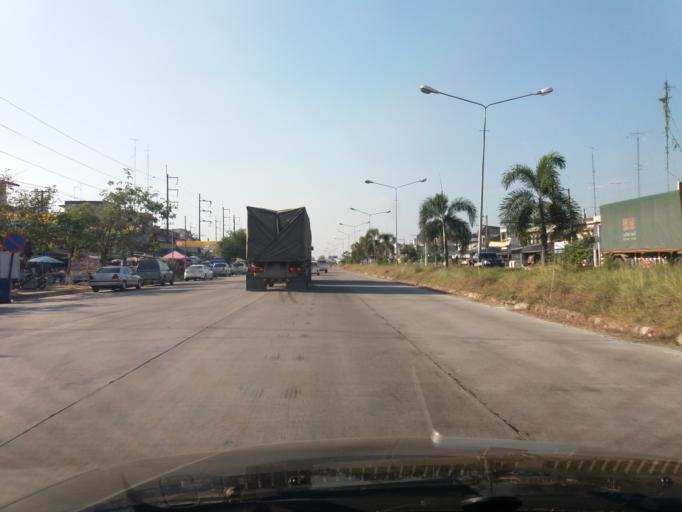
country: TH
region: Nakhon Sawan
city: Kao Liao
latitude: 15.7646
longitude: 99.9906
